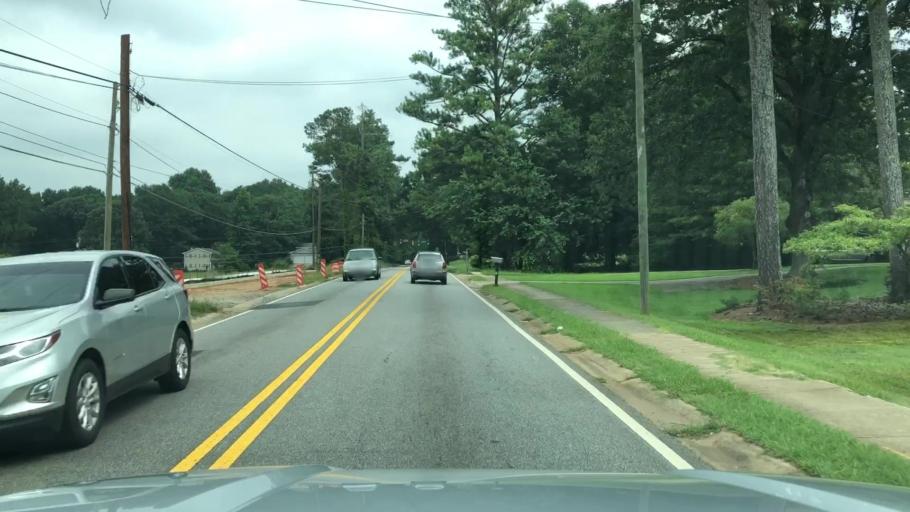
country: US
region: Georgia
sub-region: Cobb County
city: Mableton
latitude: 33.8430
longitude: -84.5783
